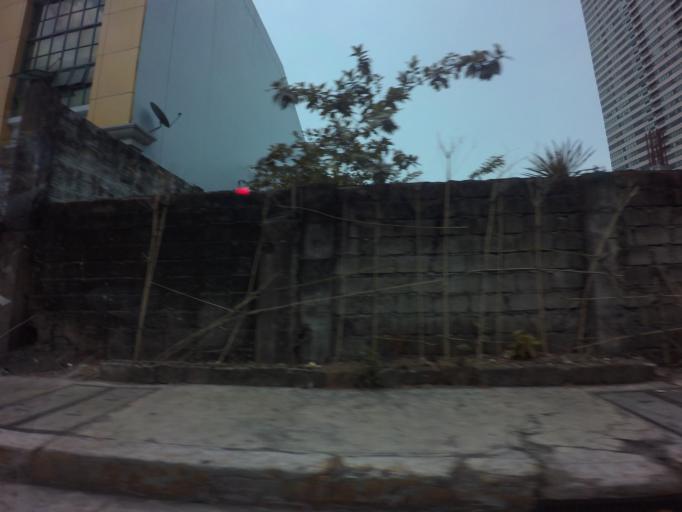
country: PH
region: Metro Manila
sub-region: Makati City
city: Makati City
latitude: 14.5643
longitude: 121.0393
